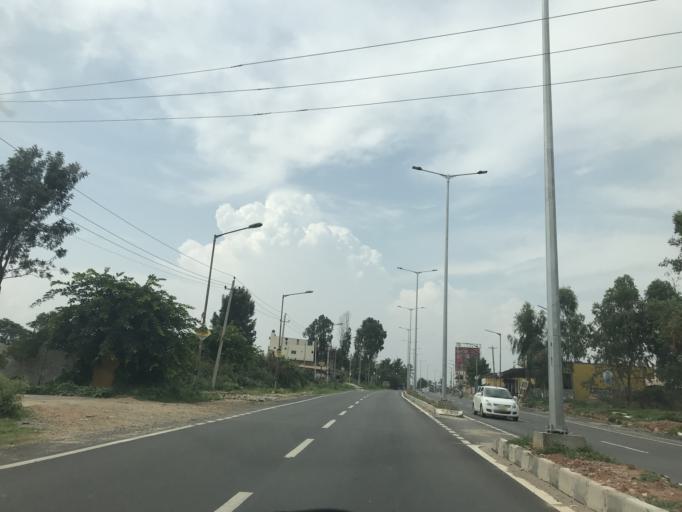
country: IN
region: Karnataka
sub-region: Bangalore Urban
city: Yelahanka
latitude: 13.1000
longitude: 77.6572
